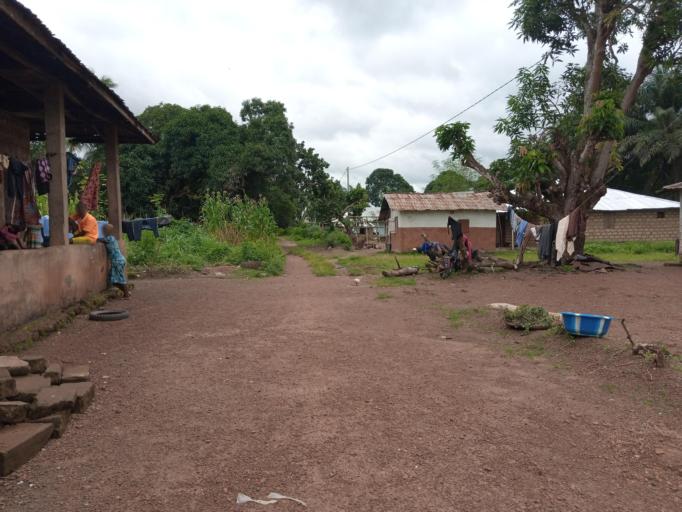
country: SL
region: Southern Province
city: Largo
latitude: 8.2029
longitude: -12.0575
